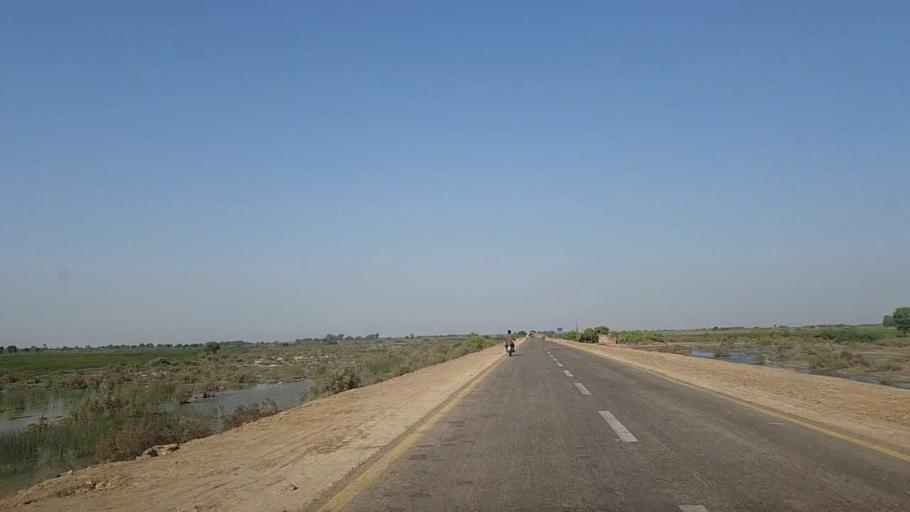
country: PK
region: Sindh
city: Jati
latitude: 24.4032
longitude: 68.2950
